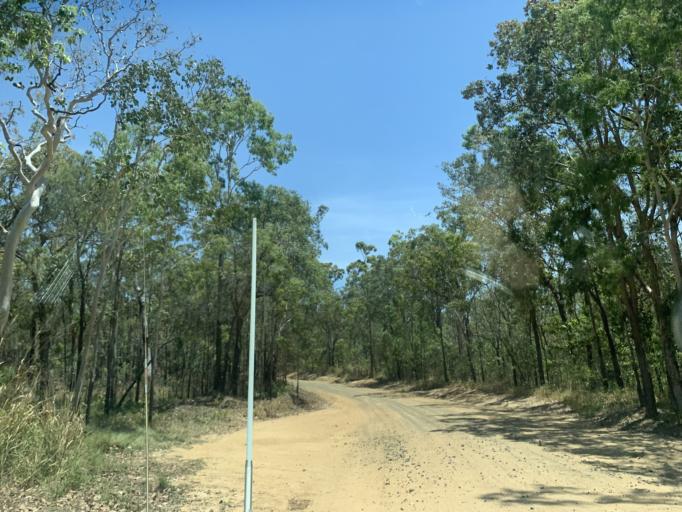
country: AU
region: Queensland
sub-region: Tablelands
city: Kuranda
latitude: -16.9189
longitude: 145.5918
